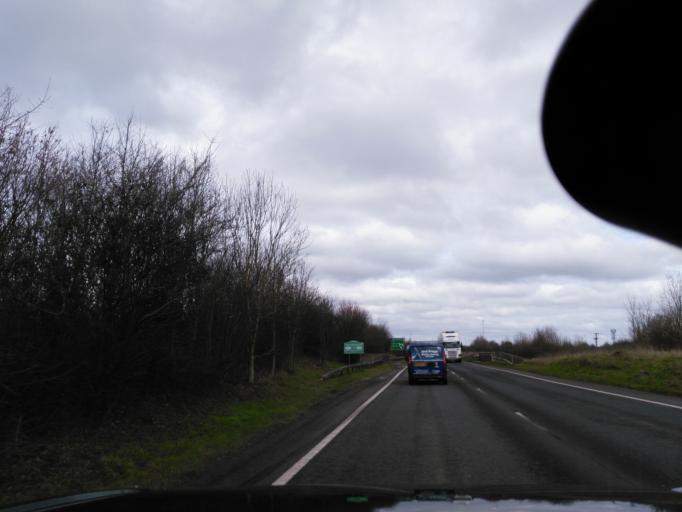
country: GB
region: England
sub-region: Wiltshire
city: Melksham
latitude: 51.3603
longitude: -2.1377
